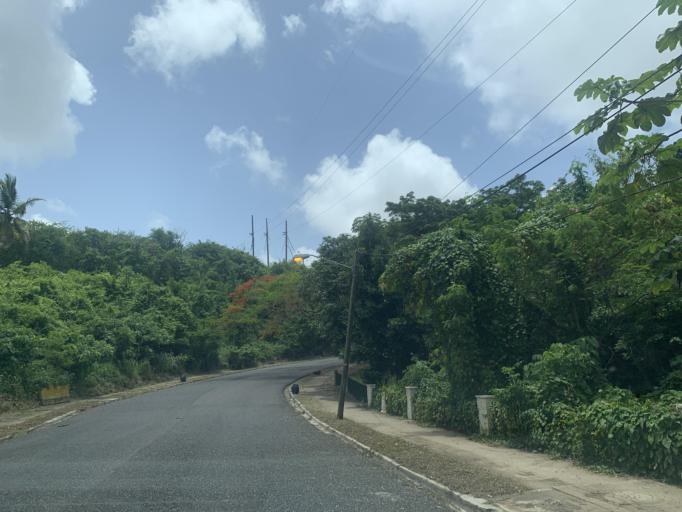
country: DO
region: Nacional
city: La Agustina
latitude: 18.5014
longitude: -69.9468
